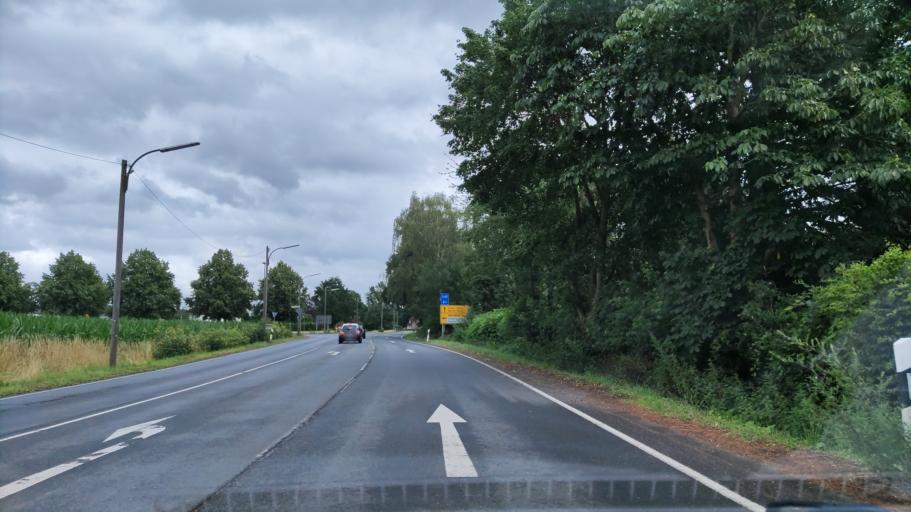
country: DE
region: North Rhine-Westphalia
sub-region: Regierungsbezirk Arnsberg
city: Hamm
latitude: 51.6704
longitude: 7.8727
